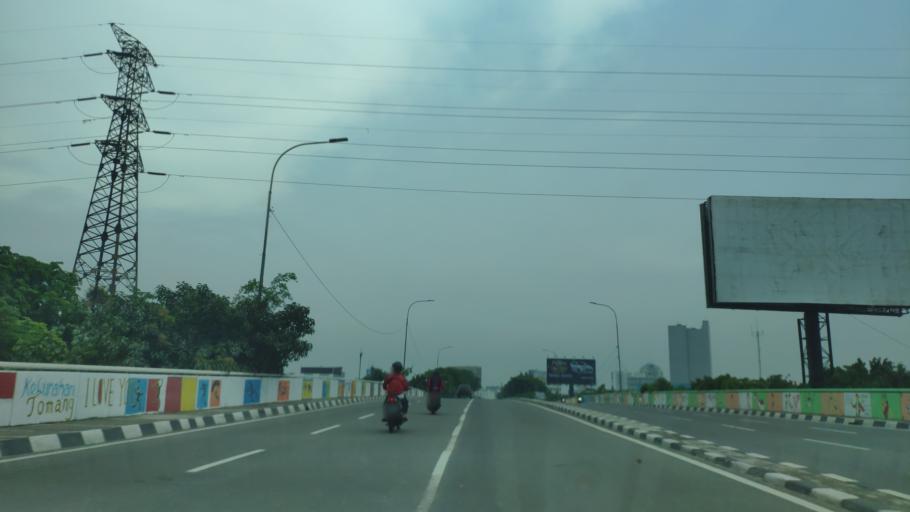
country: ID
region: Jakarta Raya
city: Jakarta
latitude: -6.1740
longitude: 106.8047
